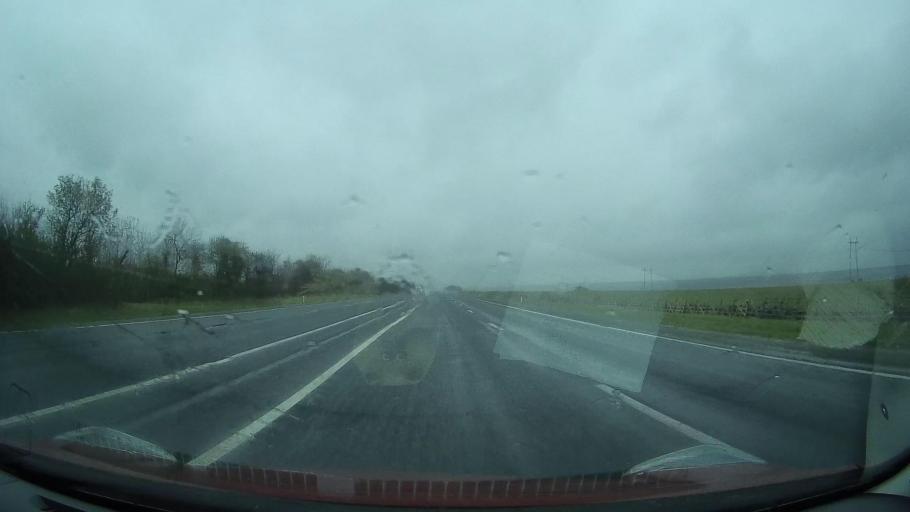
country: RU
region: Stavropol'skiy
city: Nevinnomyssk
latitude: 44.6131
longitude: 42.1152
